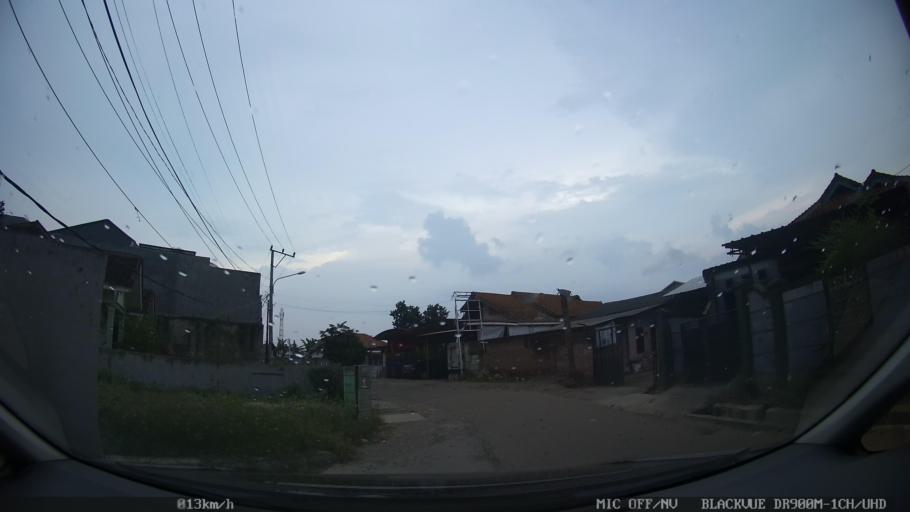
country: ID
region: Lampung
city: Kedaton
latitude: -5.3956
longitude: 105.2766
